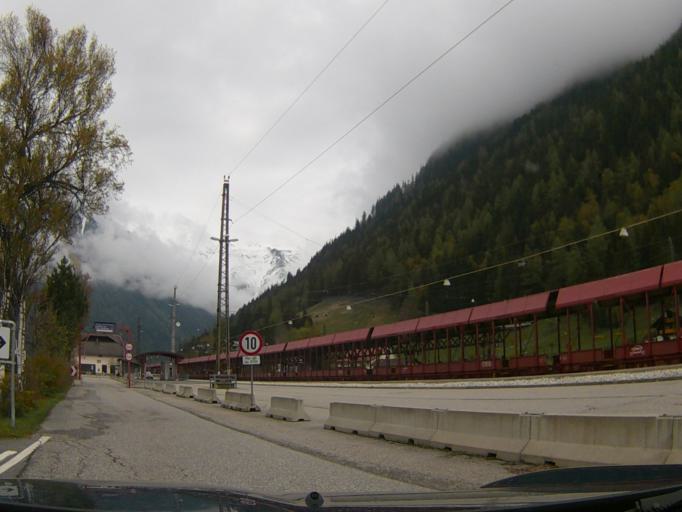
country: AT
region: Carinthia
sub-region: Politischer Bezirk Spittal an der Drau
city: Obervellach
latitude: 46.9800
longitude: 13.1766
